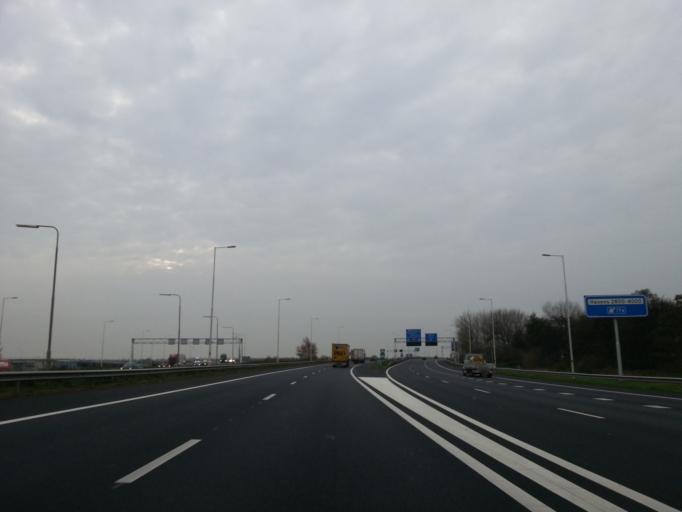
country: NL
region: South Holland
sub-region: Gemeente Schiedam
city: Schiedam
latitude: 51.8804
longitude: 4.3834
